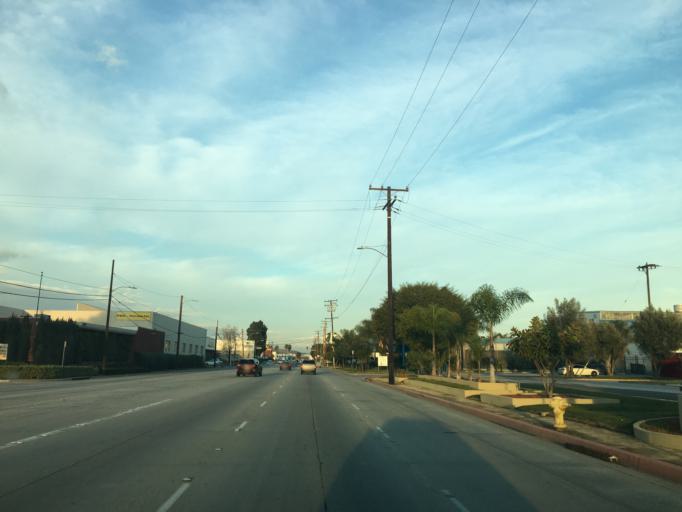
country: US
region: California
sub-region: Los Angeles County
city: Commerce
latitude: 33.9967
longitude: -118.1408
